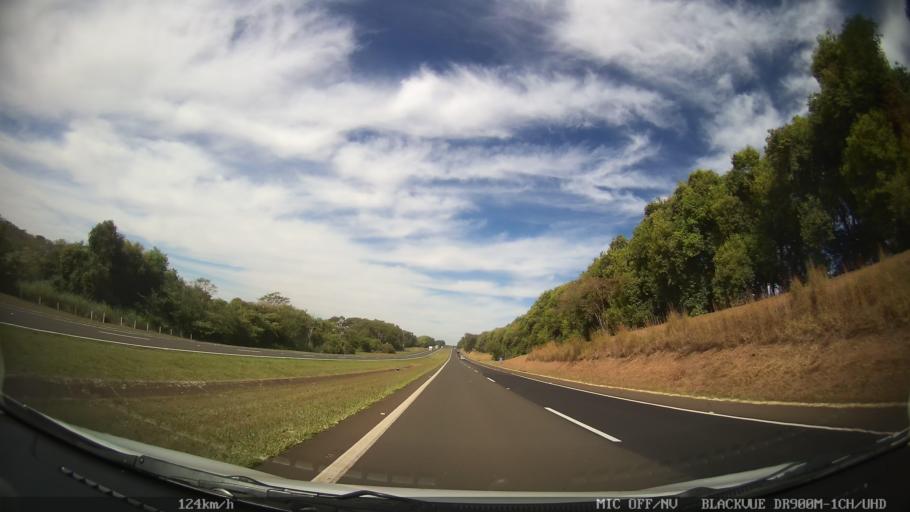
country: BR
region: Sao Paulo
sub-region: Matao
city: Matao
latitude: -21.6156
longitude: -48.4187
